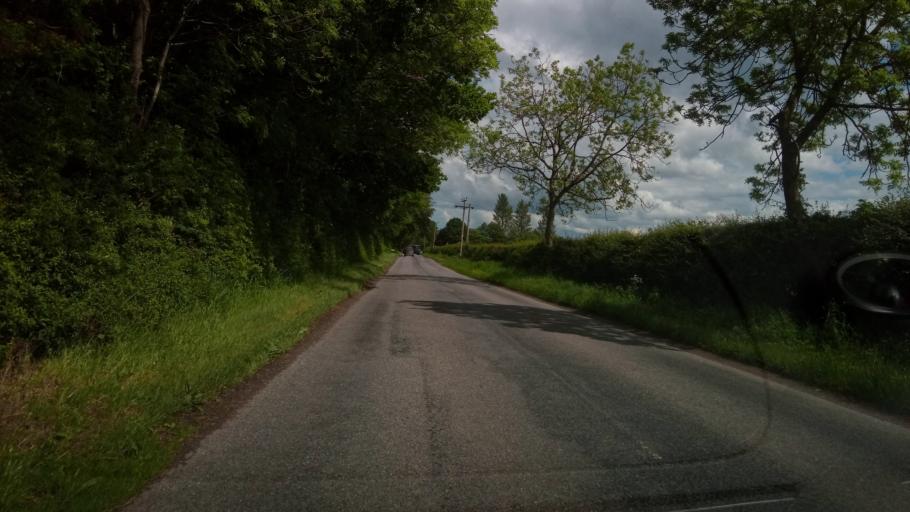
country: GB
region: Scotland
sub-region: The Scottish Borders
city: Kelso
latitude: 55.5815
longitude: -2.3901
